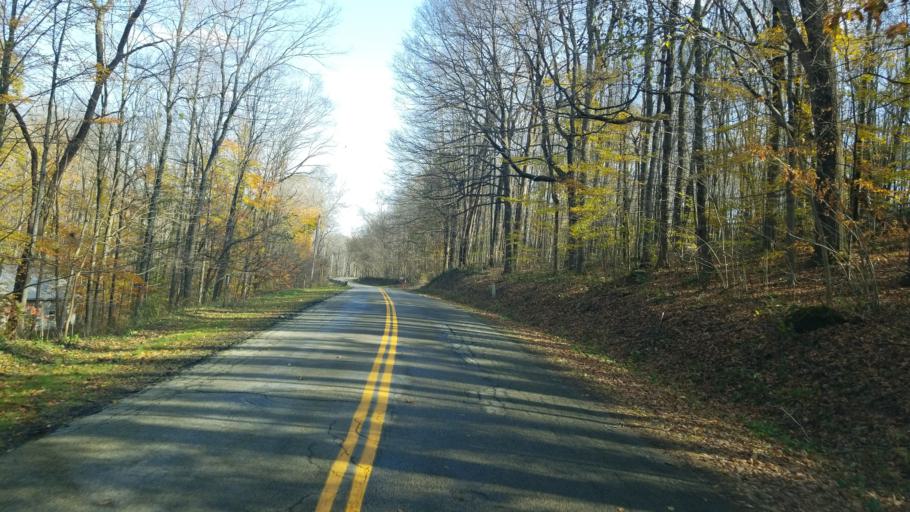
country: US
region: Ohio
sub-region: Sandusky County
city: Bellville
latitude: 40.6405
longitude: -82.4214
